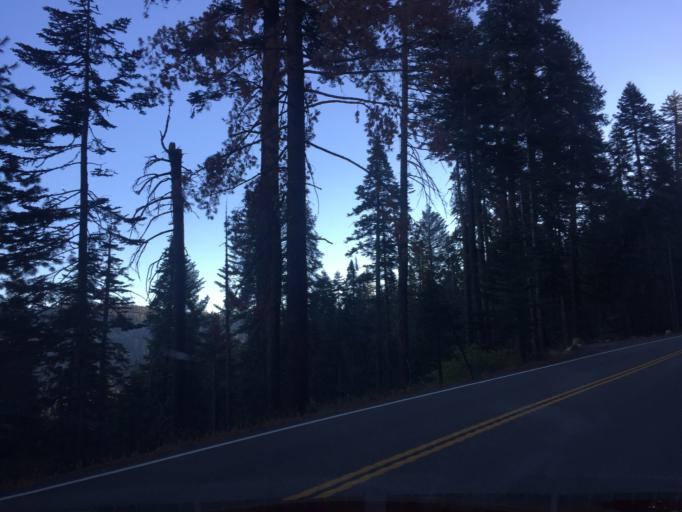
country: US
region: California
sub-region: Mariposa County
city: Yosemite Valley
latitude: 37.6740
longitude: -119.6967
